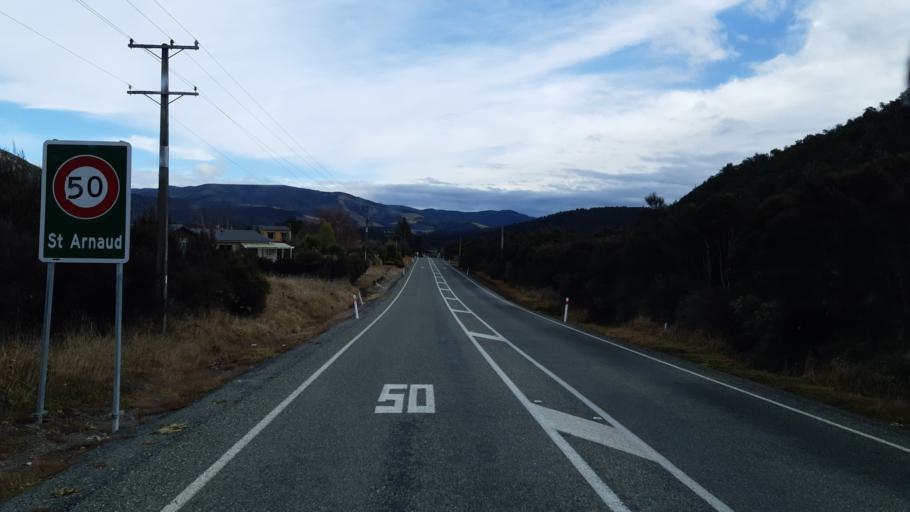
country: NZ
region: Tasman
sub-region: Tasman District
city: Wakefield
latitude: -41.8006
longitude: 172.8582
